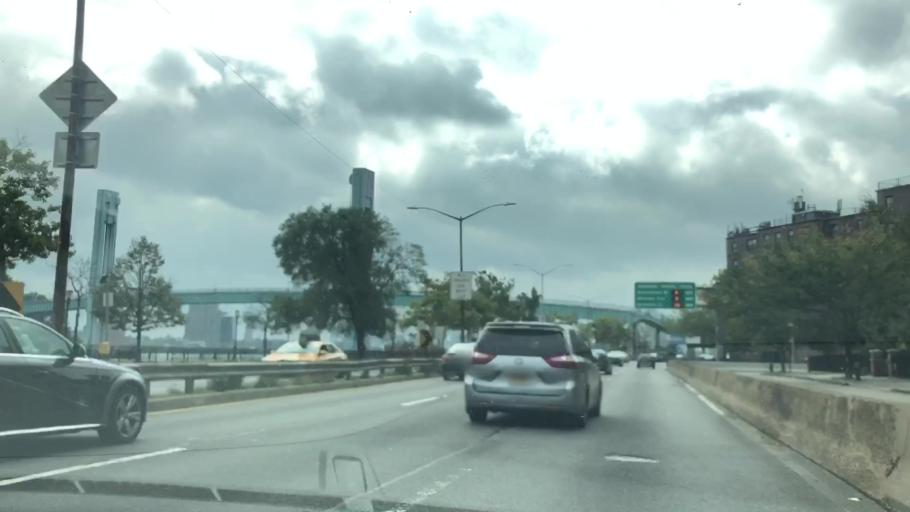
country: US
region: New York
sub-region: New York County
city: Manhattan
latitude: 40.7886
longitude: -73.9378
